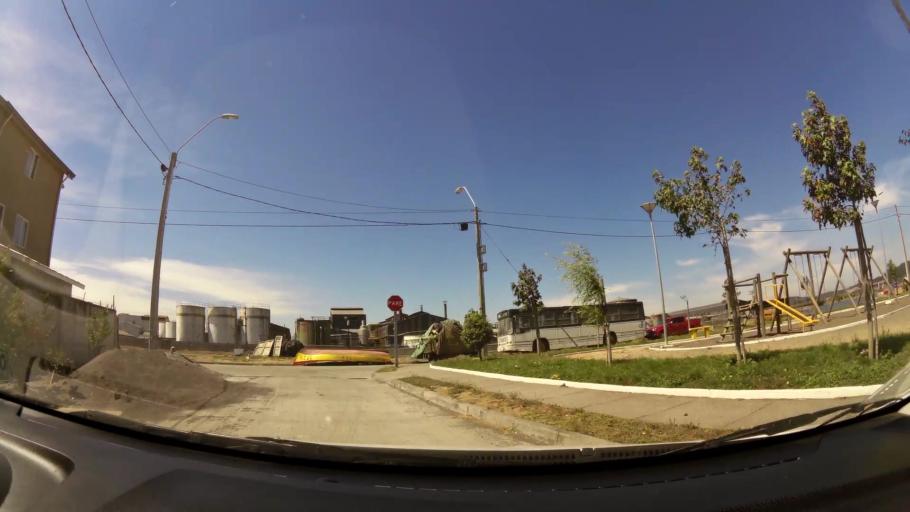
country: CL
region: Biobio
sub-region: Provincia de Concepcion
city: Talcahuano
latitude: -36.7264
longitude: -73.1053
